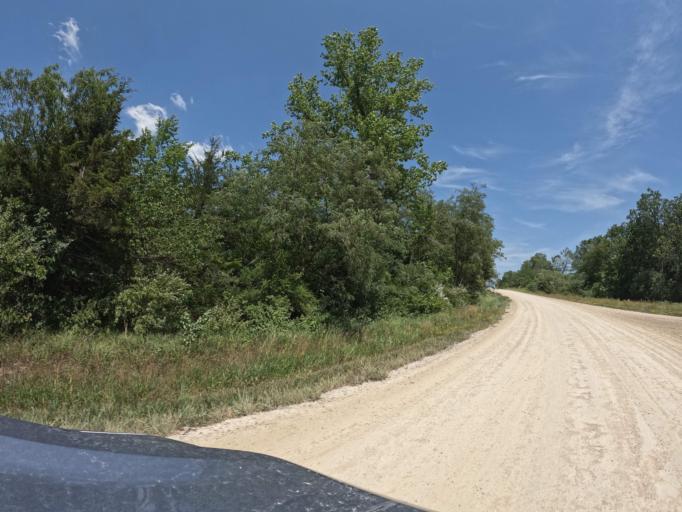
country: US
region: Iowa
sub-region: Henry County
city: Mount Pleasant
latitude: 40.9578
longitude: -91.5930
